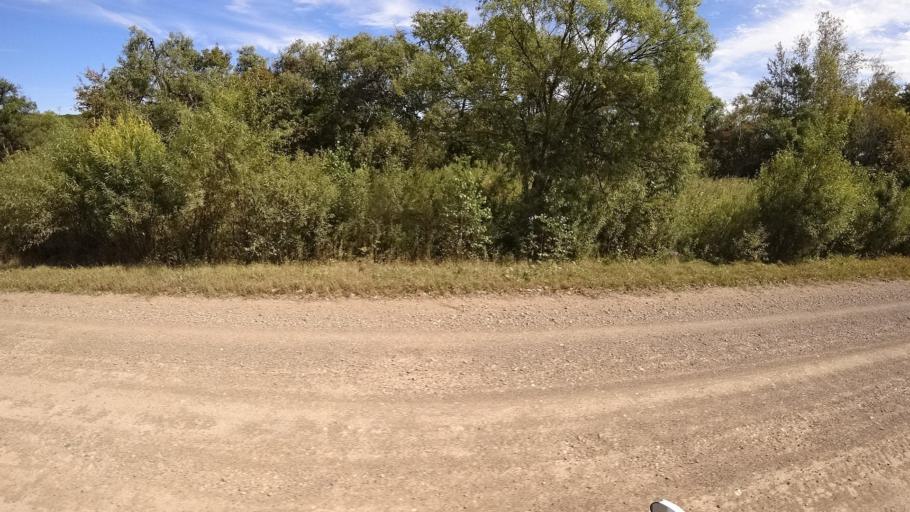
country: RU
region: Primorskiy
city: Yakovlevka
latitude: 44.7209
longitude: 133.6149
